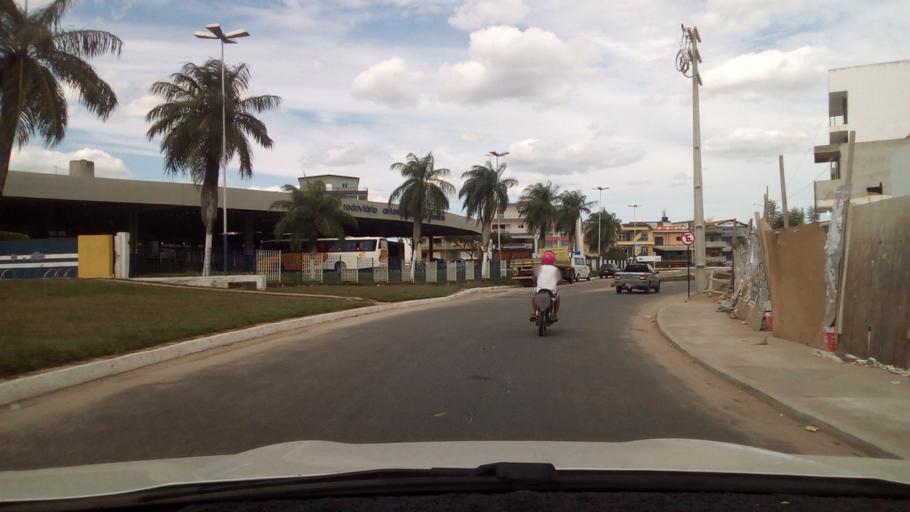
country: BR
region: Paraiba
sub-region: Guarabira
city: Guarabira
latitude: -6.8547
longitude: -35.4961
